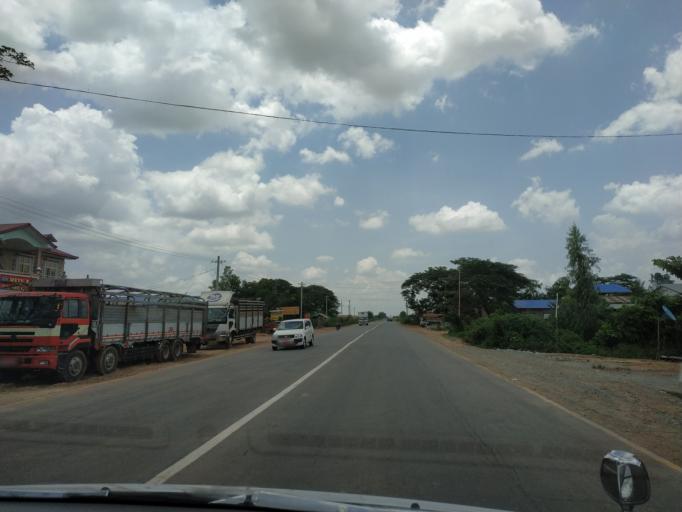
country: MM
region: Bago
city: Bago
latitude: 17.4710
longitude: 96.5504
